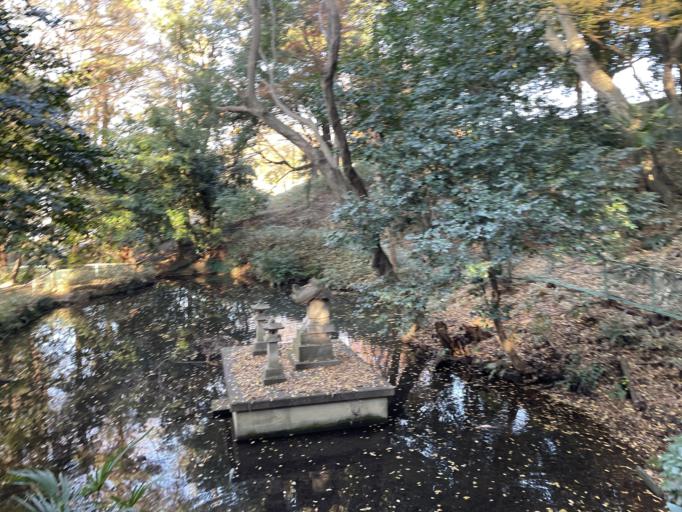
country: JP
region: Saitama
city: Asaka
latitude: 35.7870
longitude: 139.5825
